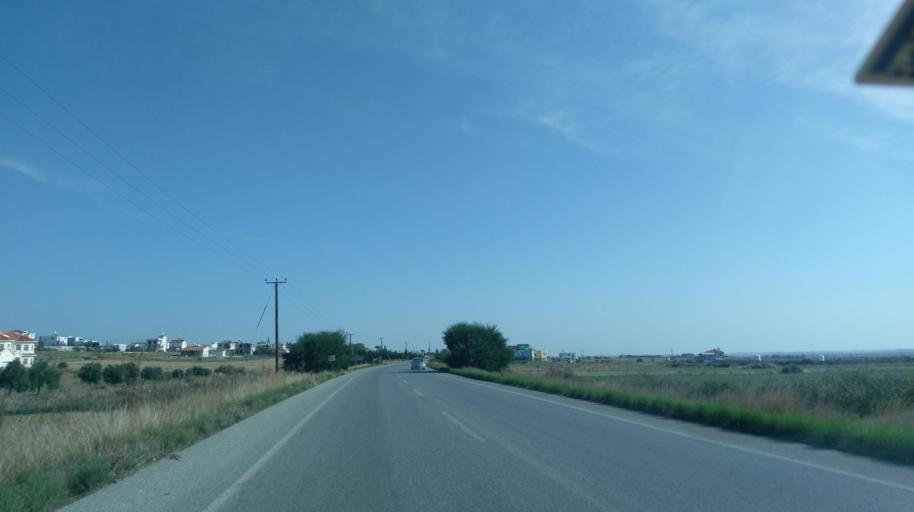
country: CY
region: Ammochostos
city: Lefkonoiko
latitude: 35.2419
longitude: 33.5930
